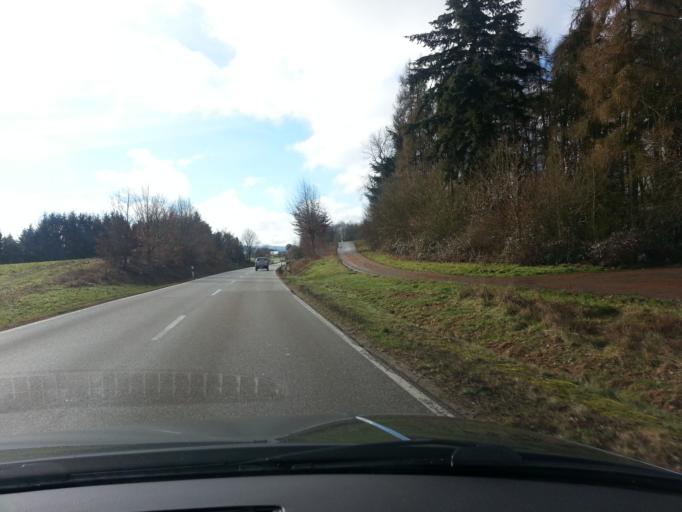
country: DE
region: Rheinland-Pfalz
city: Schwedelbach
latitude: 49.4866
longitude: 7.5900
